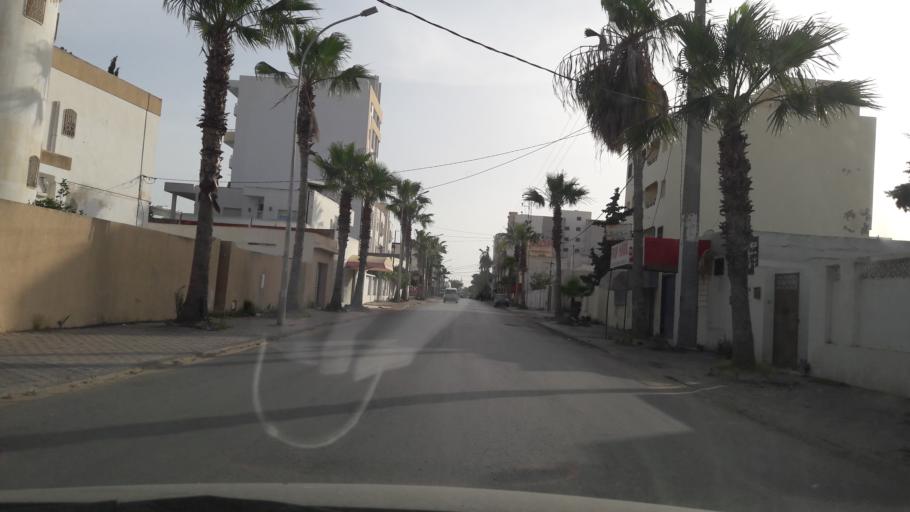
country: TN
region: Safaqis
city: Al Qarmadah
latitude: 34.8013
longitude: 10.7588
